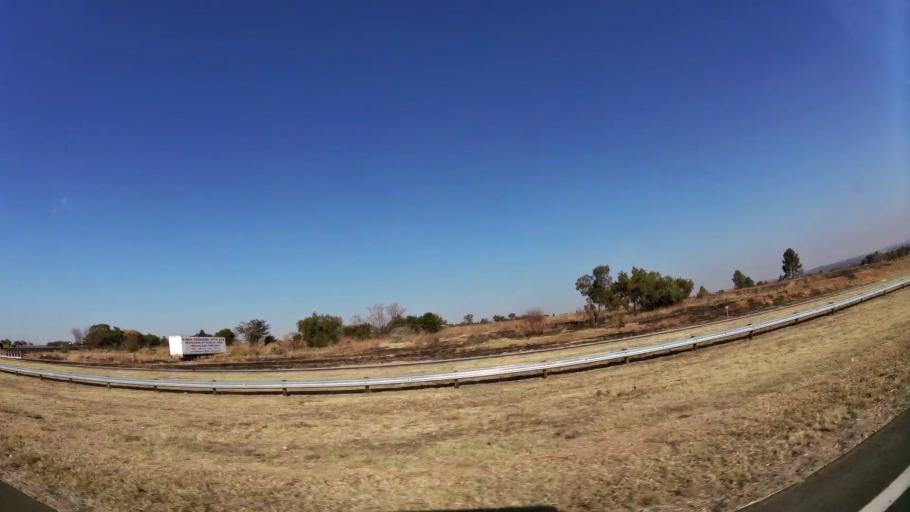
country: ZA
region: Gauteng
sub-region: West Rand District Municipality
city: Muldersdriseloop
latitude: -25.9928
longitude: 27.9123
